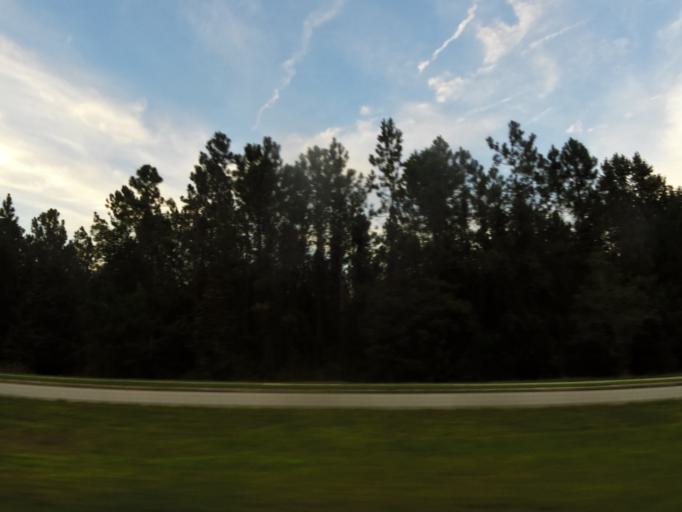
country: US
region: Florida
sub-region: Saint Johns County
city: Fruit Cove
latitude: 30.0852
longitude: -81.5693
